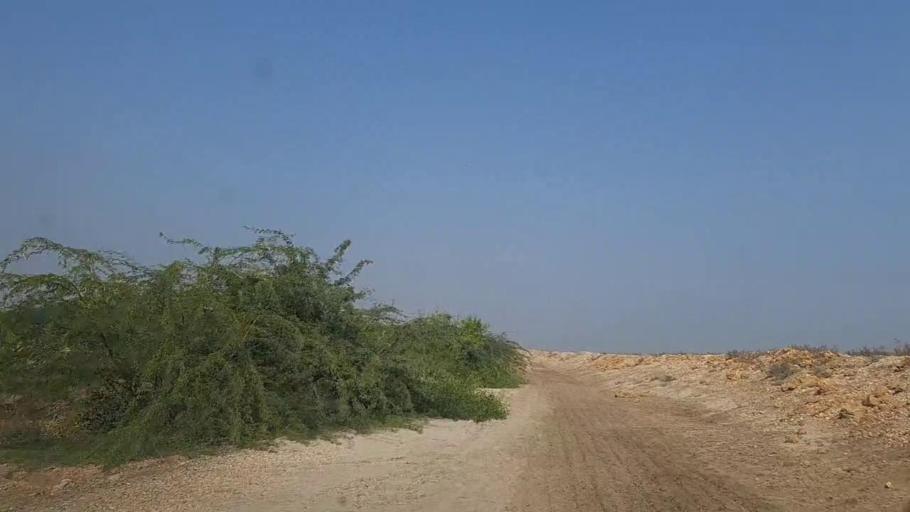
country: PK
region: Sindh
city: Thatta
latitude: 24.6580
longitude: 67.9271
